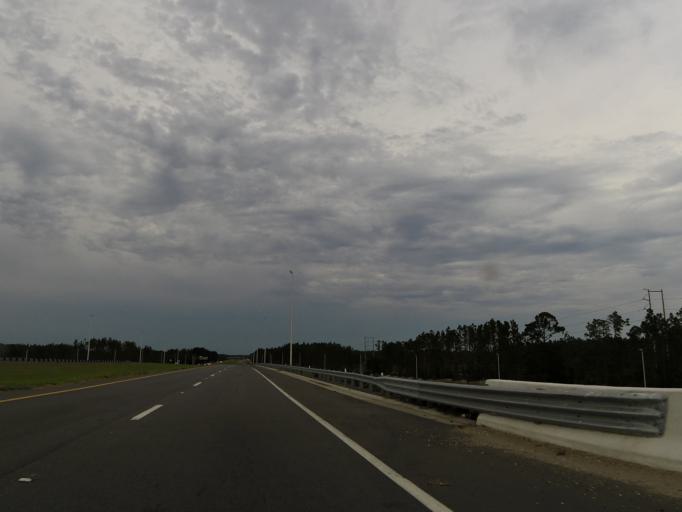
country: US
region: Florida
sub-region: Clay County
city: Bellair-Meadowbrook Terrace
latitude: 30.1959
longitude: -81.8373
